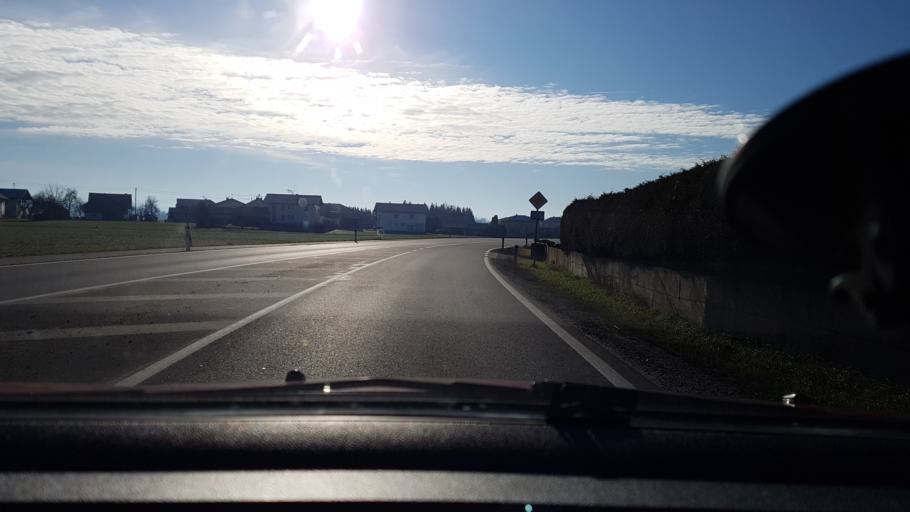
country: AT
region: Upper Austria
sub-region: Politischer Bezirk Braunau am Inn
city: Braunau am Inn
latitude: 48.1857
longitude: 13.0575
